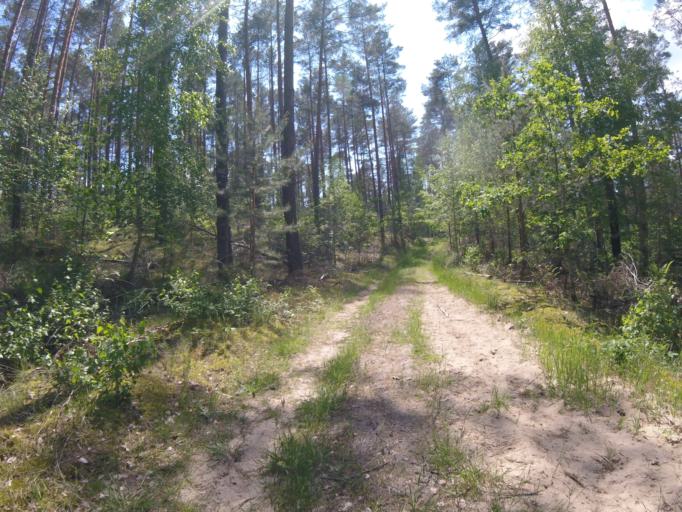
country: DE
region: Brandenburg
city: Teupitz
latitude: 52.1046
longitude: 13.5949
